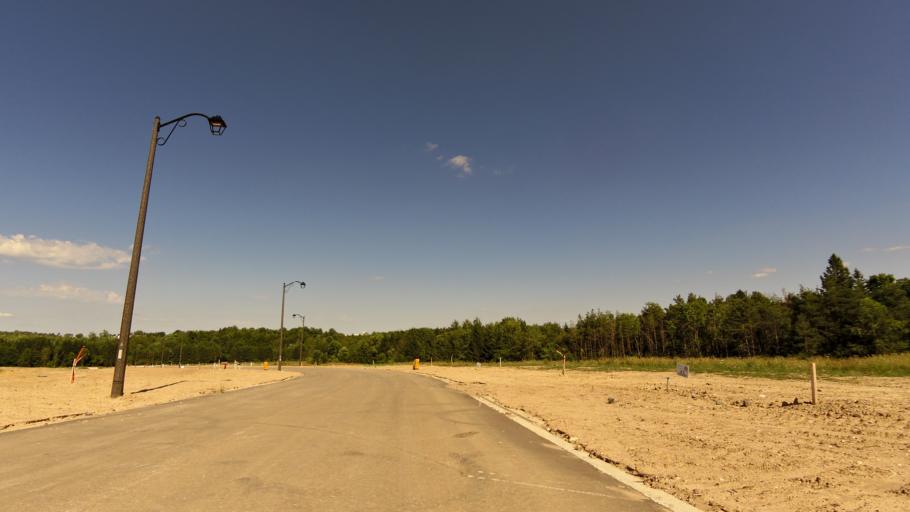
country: CA
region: Ontario
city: Brampton
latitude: 43.7587
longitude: -79.9274
